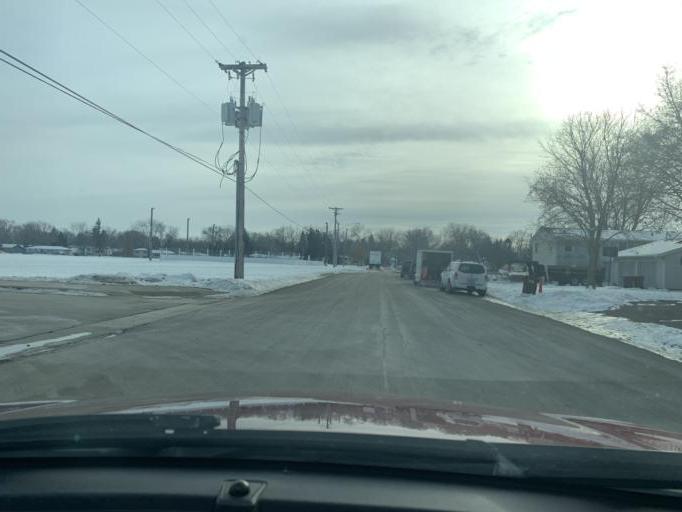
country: US
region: Minnesota
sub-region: Washington County
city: Saint Paul Park
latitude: 44.8355
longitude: -92.9827
